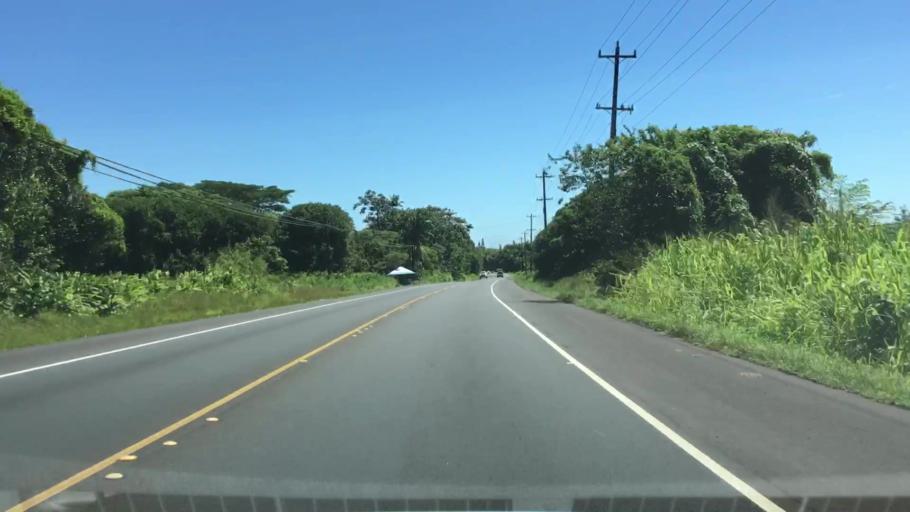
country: US
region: Hawaii
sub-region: Hawaii County
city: Kurtistown
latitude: 19.5724
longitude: -155.0756
